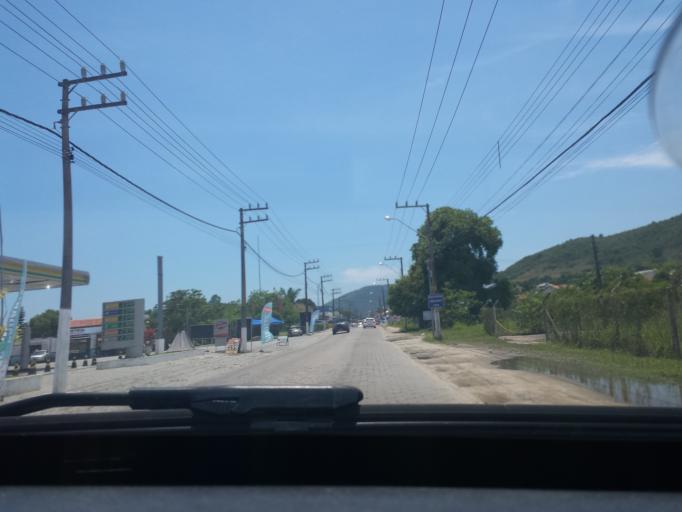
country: BR
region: Santa Catarina
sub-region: Porto Belo
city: Porto Belo
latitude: -27.1591
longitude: -48.5679
